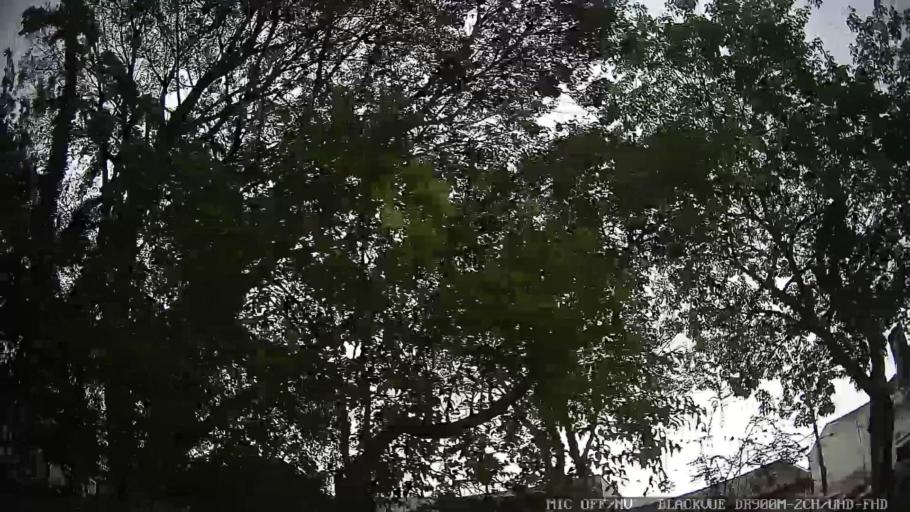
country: BR
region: Sao Paulo
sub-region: Caieiras
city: Caieiras
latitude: -23.4514
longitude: -46.7459
